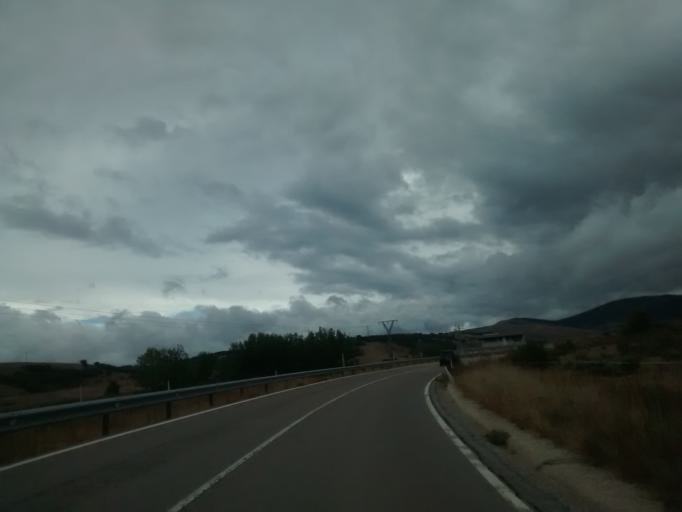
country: ES
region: Cantabria
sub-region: Provincia de Cantabria
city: Mataporquera
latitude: 42.8790
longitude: -4.0701
